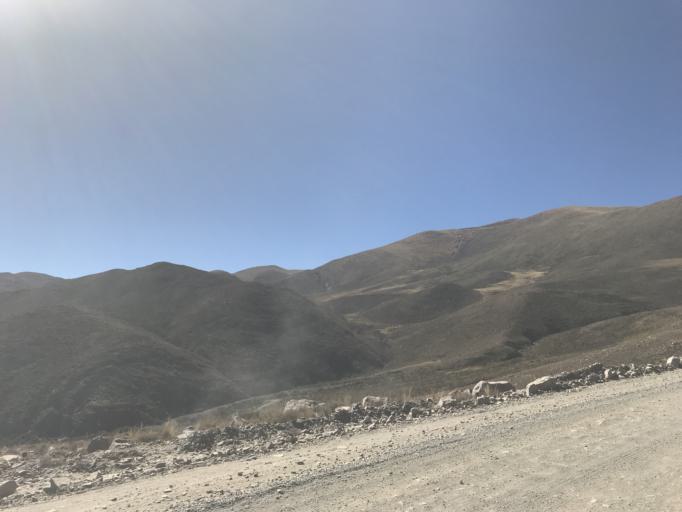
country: AR
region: Jujuy
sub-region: Departamento de Humahuaca
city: Humahuaca
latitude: -23.1967
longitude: -65.2239
